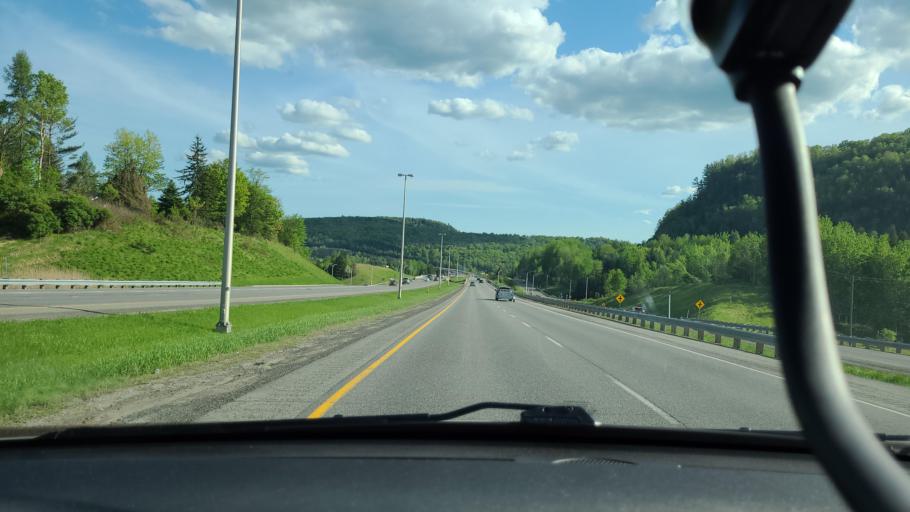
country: CA
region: Quebec
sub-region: Laurentides
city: Sainte-Adele
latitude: 45.9252
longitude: -74.1474
